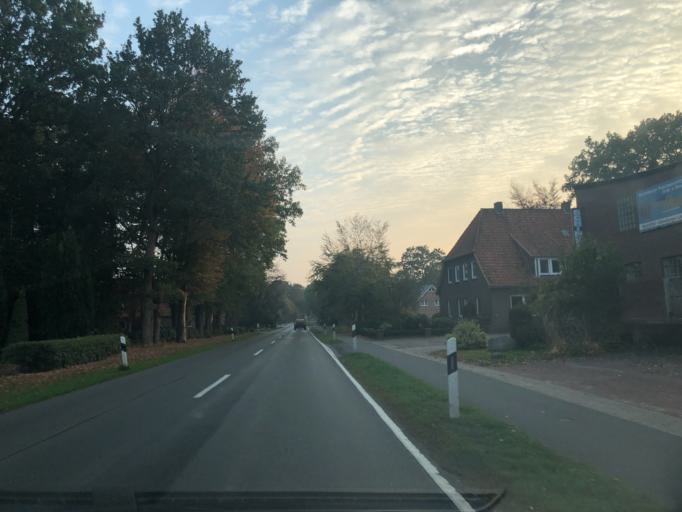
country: DE
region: Lower Saxony
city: Wardenburg
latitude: 53.0581
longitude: 8.1595
